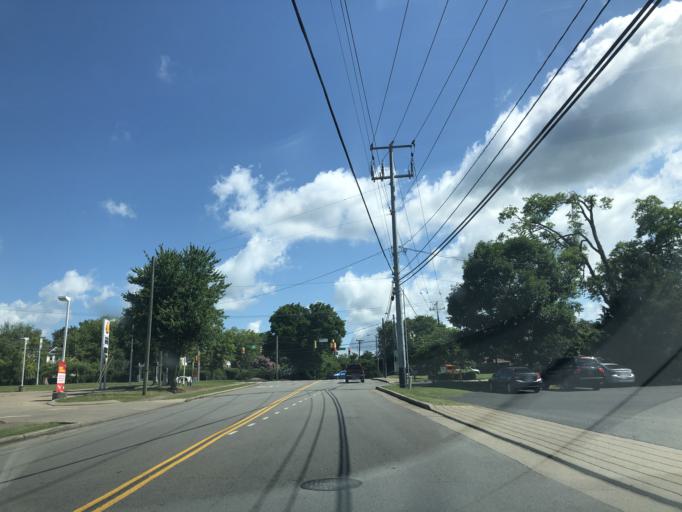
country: US
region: Tennessee
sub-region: Davidson County
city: Belle Meade
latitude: 36.0731
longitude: -86.9264
